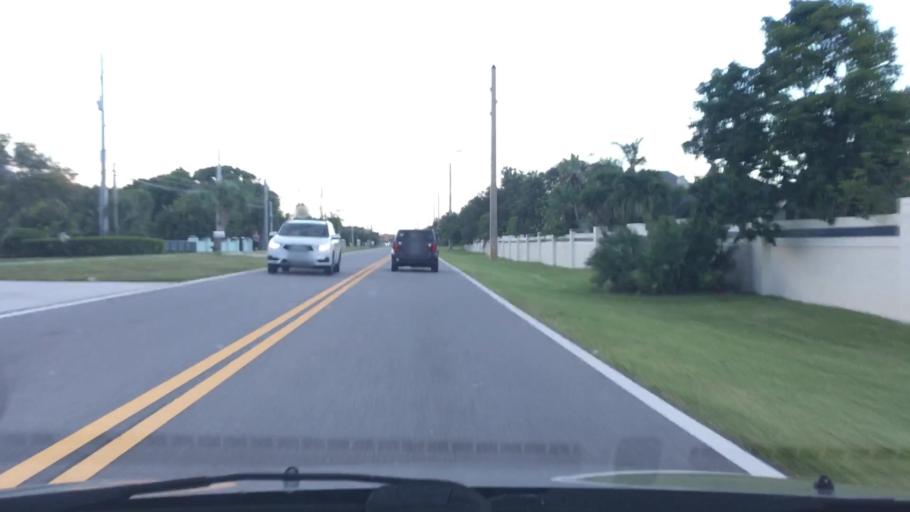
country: US
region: Florida
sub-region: Brevard County
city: Indian Harbour Beach
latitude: 28.1264
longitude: -80.5898
